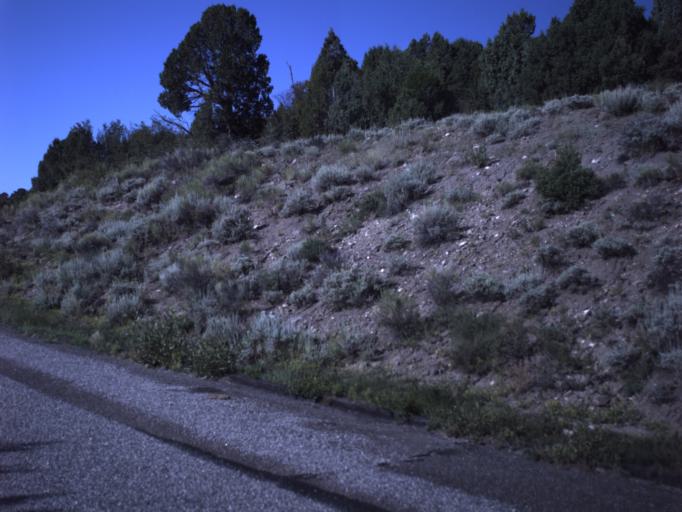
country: US
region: Utah
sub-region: Wayne County
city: Loa
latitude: 38.6126
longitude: -111.4599
